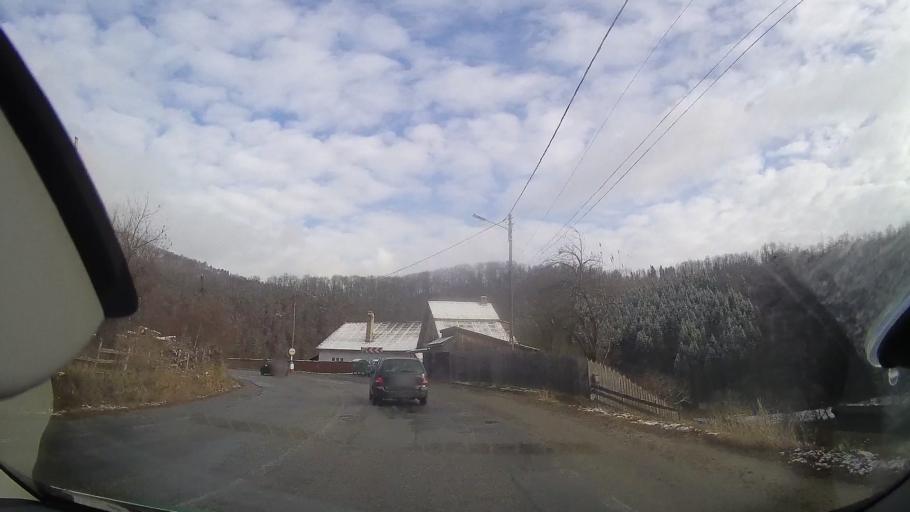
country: RO
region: Alba
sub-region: Oras Baia de Aries
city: Baia de Aries
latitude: 46.3766
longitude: 23.2609
